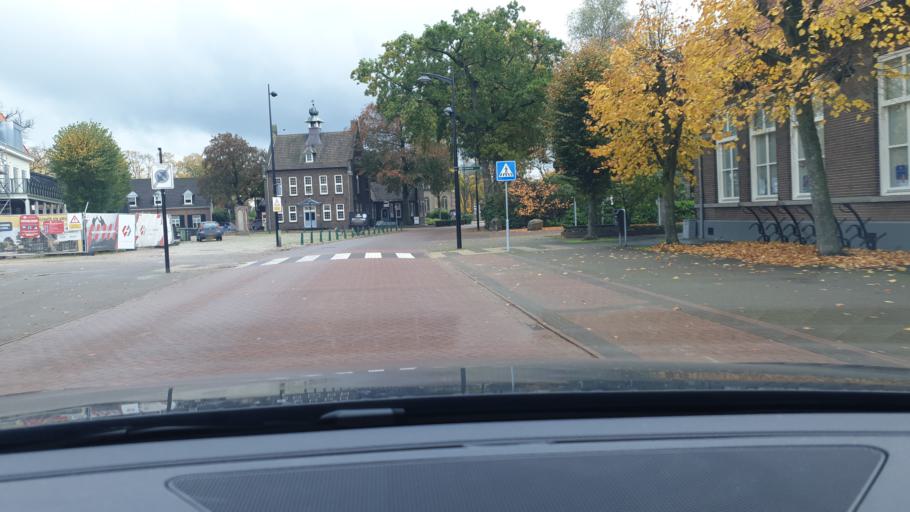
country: NL
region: North Brabant
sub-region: Gemeente Bernheze
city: Heesch
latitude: 51.7021
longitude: 5.5619
